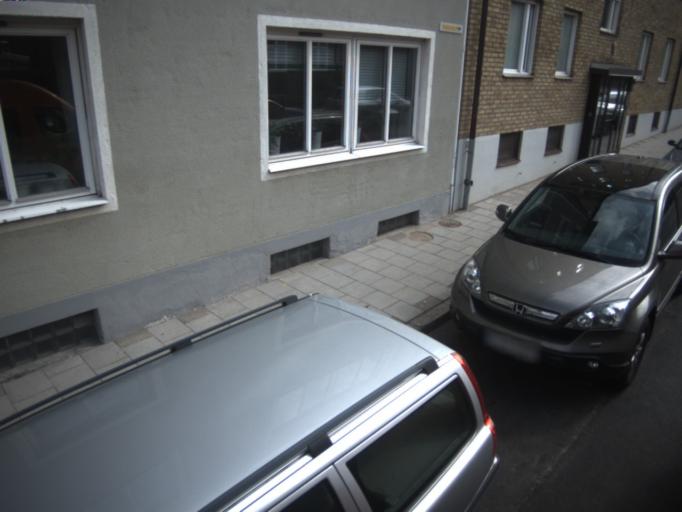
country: SE
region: Skane
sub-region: Helsingborg
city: Helsingborg
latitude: 56.0562
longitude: 12.6931
